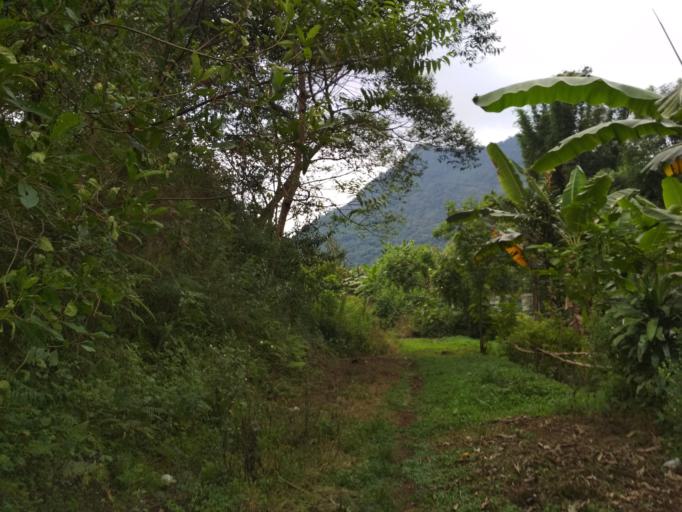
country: MX
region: Veracruz
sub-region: Fortin
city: Santa Lucia Potrerillo
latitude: 18.9545
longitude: -97.0448
